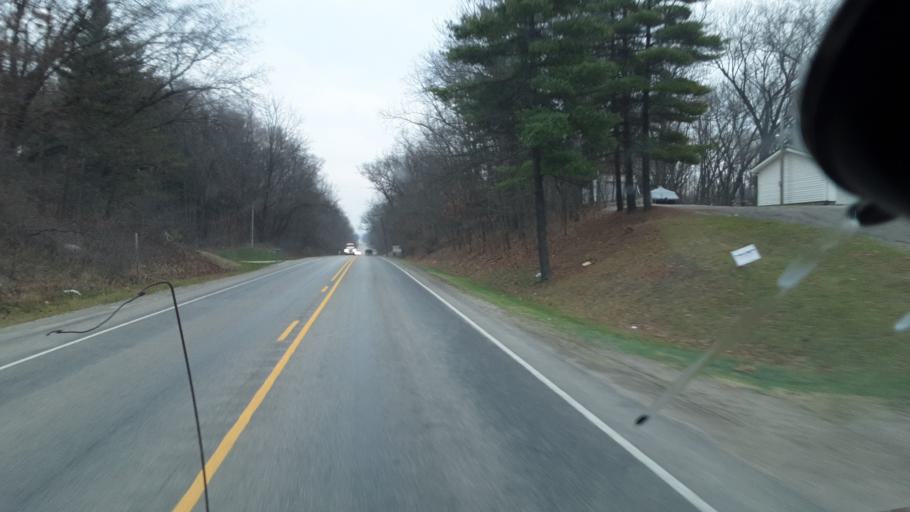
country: US
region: Michigan
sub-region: Saint Joseph County
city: White Pigeon
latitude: 41.7261
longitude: -85.6425
